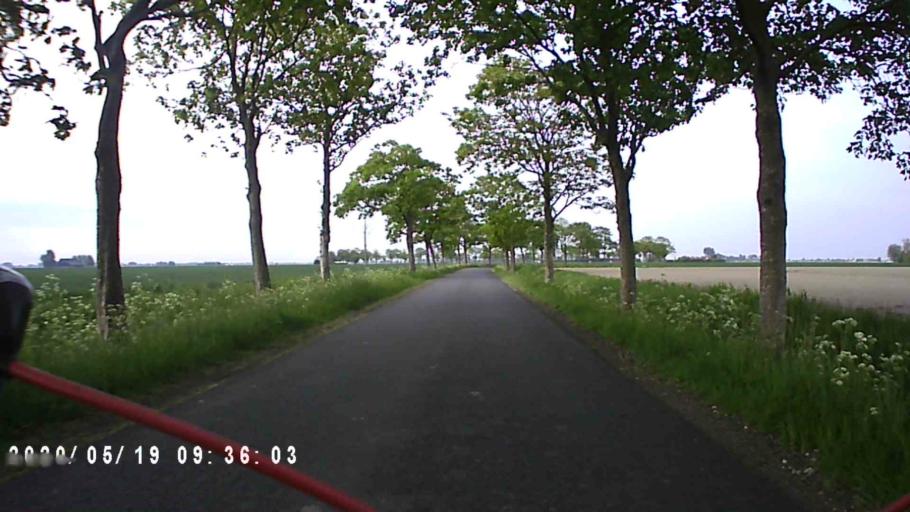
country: NL
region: Groningen
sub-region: Gemeente Zuidhorn
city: Grijpskerk
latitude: 53.2943
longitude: 6.2869
